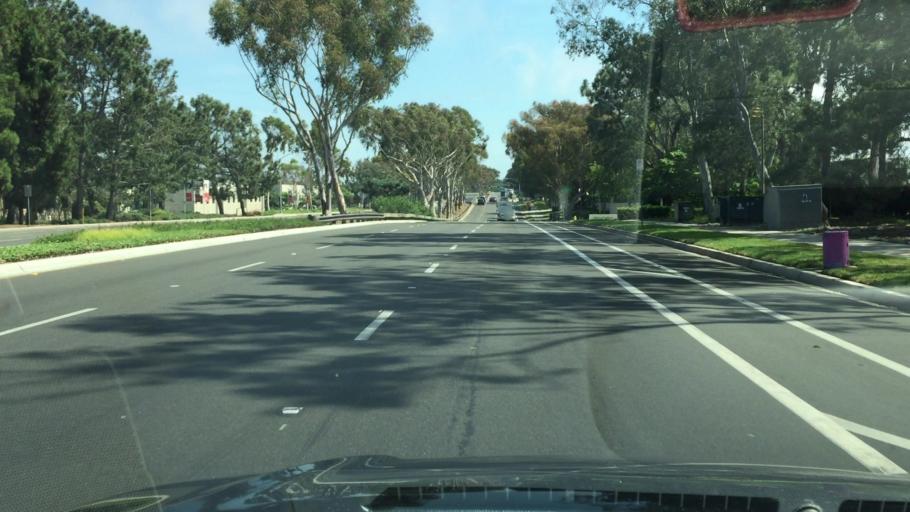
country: US
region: California
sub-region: San Diego County
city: Del Mar
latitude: 32.9014
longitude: -117.2428
